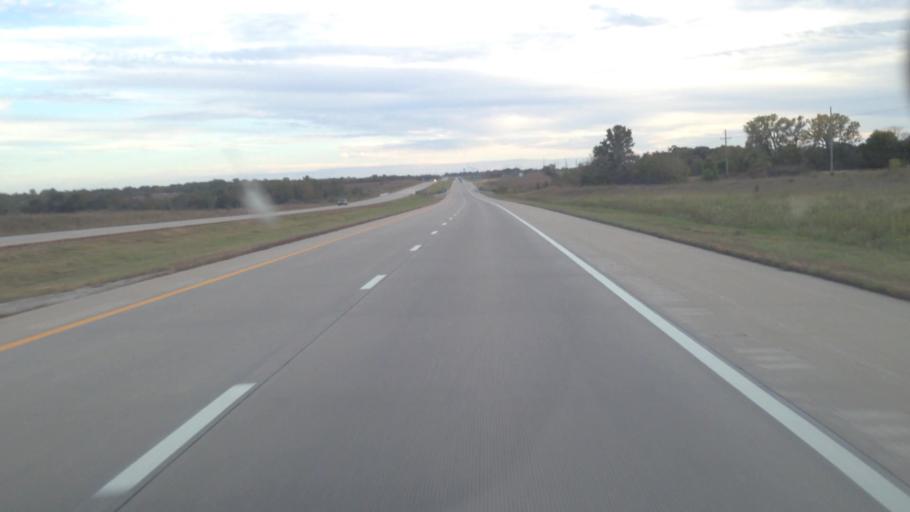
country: US
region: Kansas
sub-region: Douglas County
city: Baldwin City
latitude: 38.7293
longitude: -95.2686
